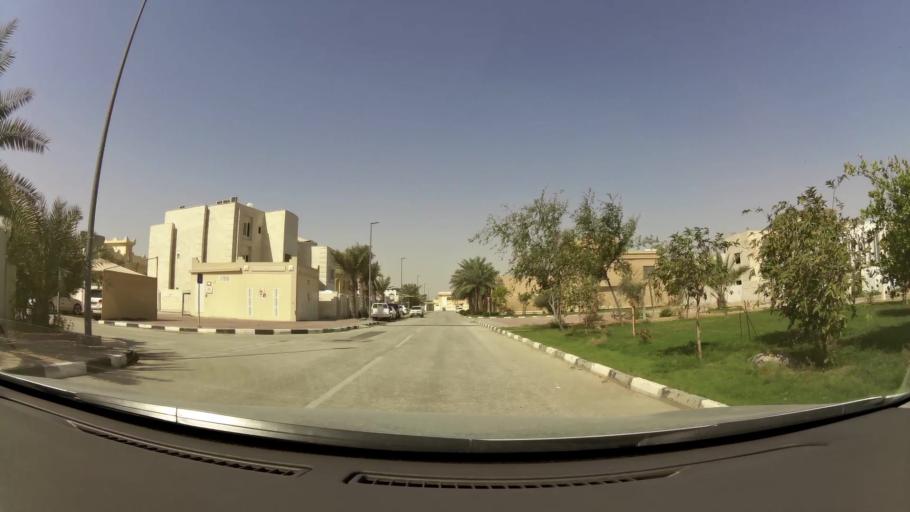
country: QA
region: Baladiyat ad Dawhah
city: Doha
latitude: 25.3640
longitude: 51.4978
